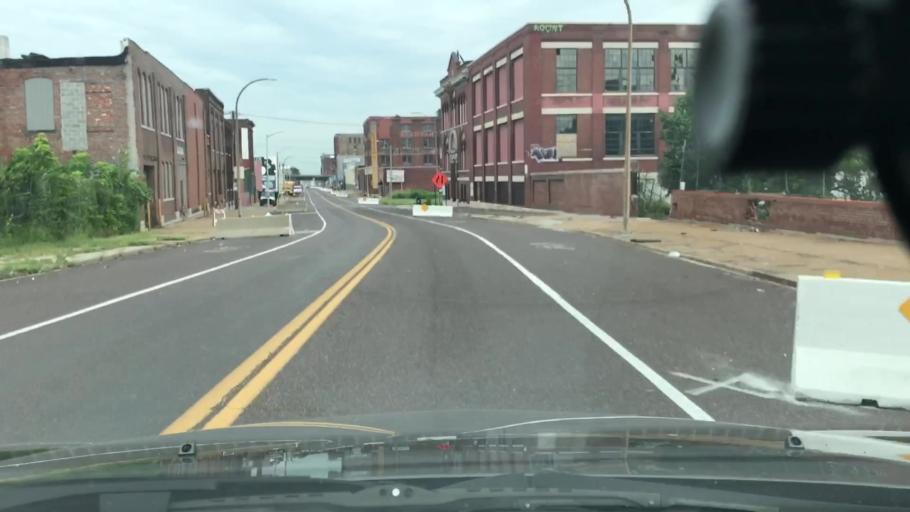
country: US
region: Missouri
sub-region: City of Saint Louis
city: St. Louis
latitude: 38.6455
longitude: -90.1869
